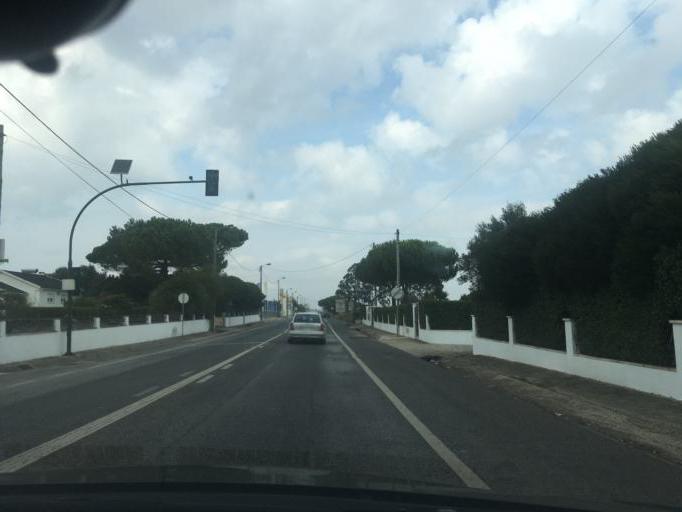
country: PT
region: Lisbon
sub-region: Sintra
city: Sintra
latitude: 38.8280
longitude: -9.3575
